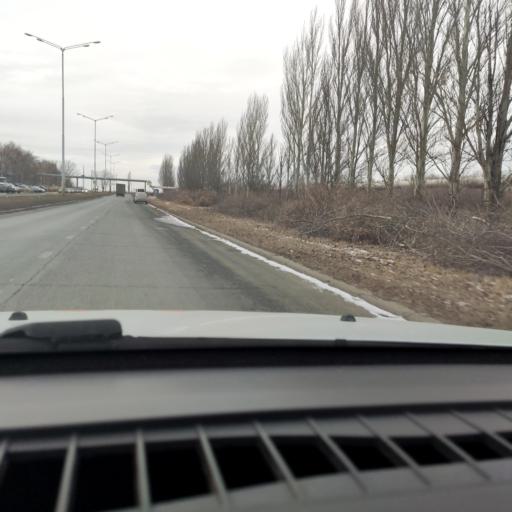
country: RU
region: Samara
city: Podstepki
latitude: 53.5725
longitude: 49.2245
